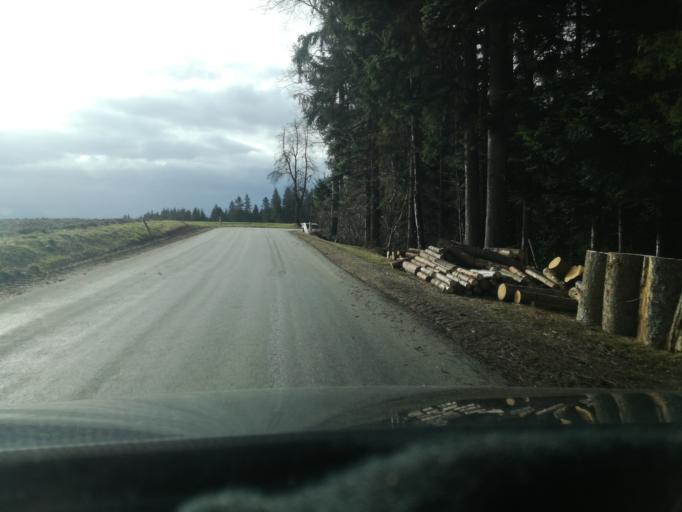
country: AT
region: Upper Austria
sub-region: Politischer Bezirk Vocklabruck
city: Frankenburg
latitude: 48.1032
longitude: 13.4650
